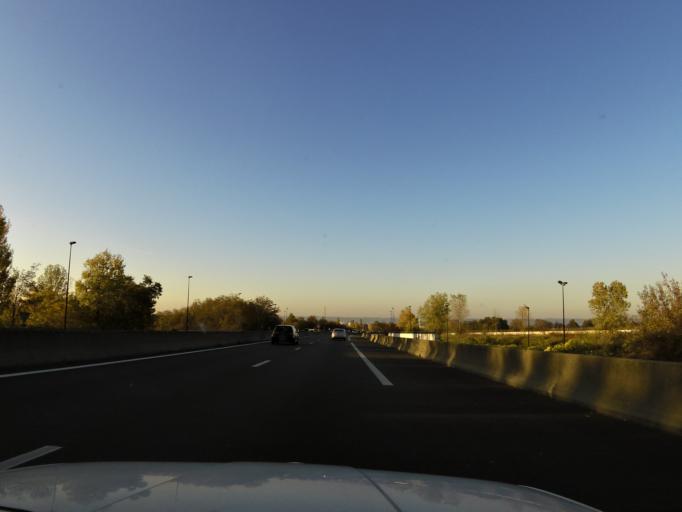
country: FR
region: Rhone-Alpes
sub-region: Departement du Rhone
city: Chassieu
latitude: 45.7494
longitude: 4.9872
